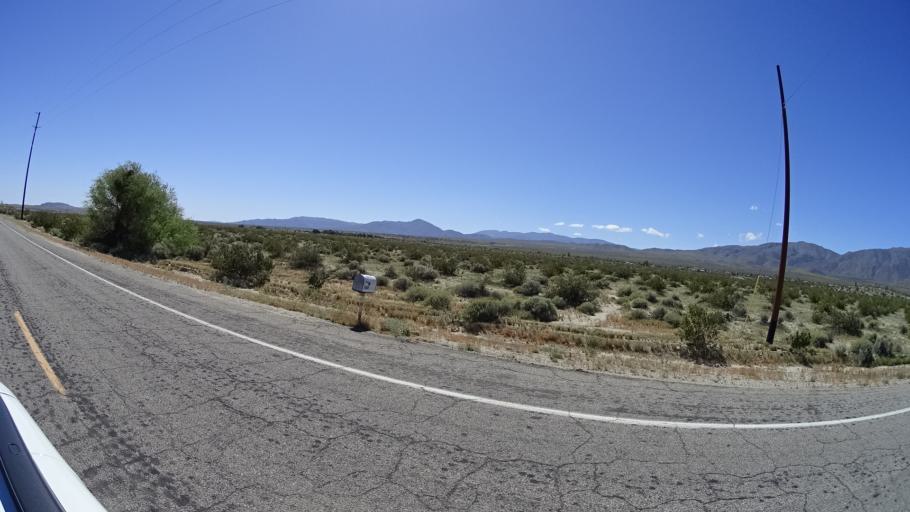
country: US
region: California
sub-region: San Diego County
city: Borrego Springs
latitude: 33.2208
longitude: -116.3375
